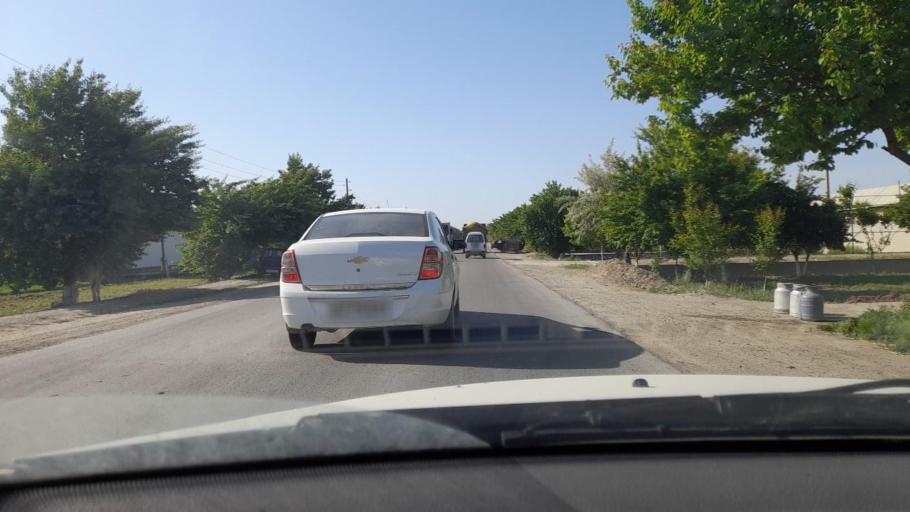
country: UZ
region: Bukhara
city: Romiton
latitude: 40.0581
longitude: 64.3278
